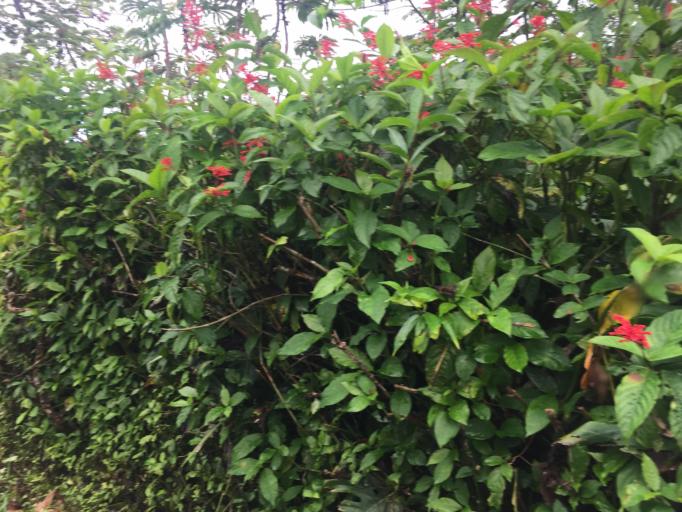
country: US
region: Hawaii
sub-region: Hawaii County
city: Pepeekeo
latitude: 19.8545
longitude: -155.1534
